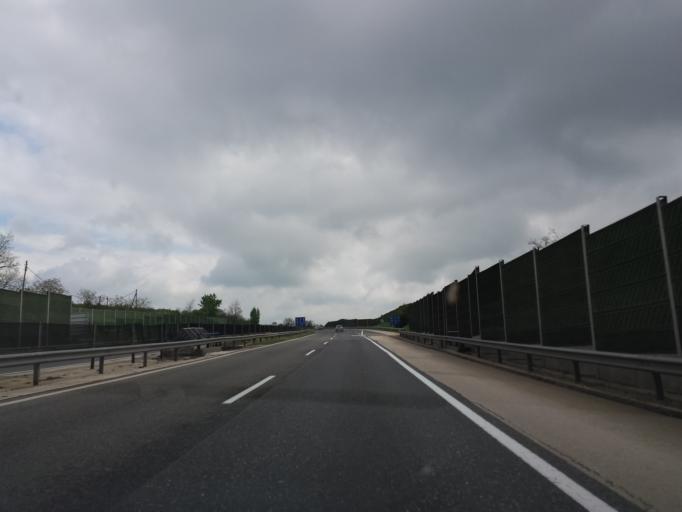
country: HU
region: Fejer
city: Szarliget
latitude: 47.4951
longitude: 18.5671
